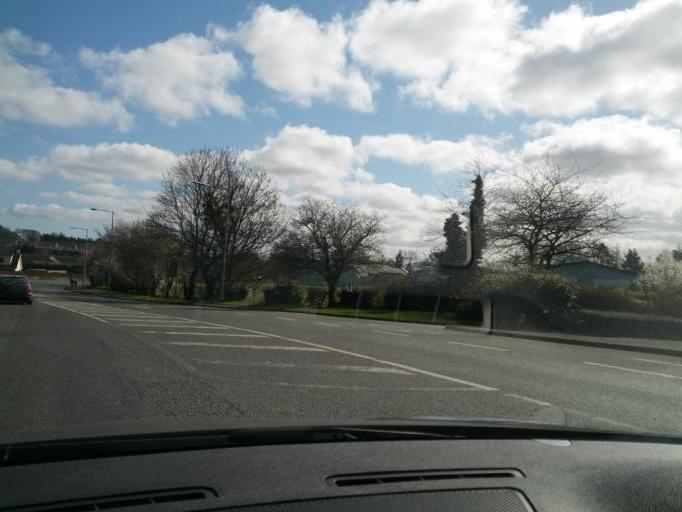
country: IE
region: Leinster
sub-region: Kildare
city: Leixlip
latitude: 53.3668
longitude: -6.4968
